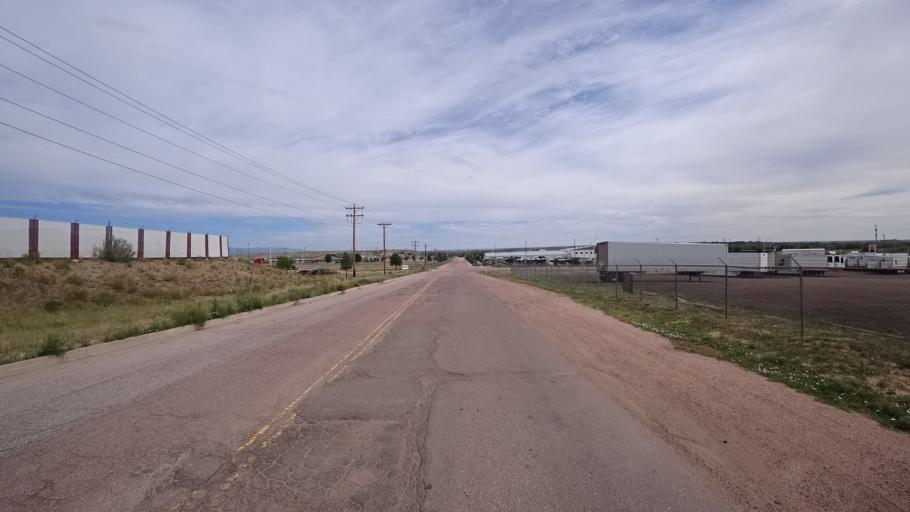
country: US
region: Colorado
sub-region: El Paso County
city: Fountain
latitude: 38.6705
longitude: -104.7149
